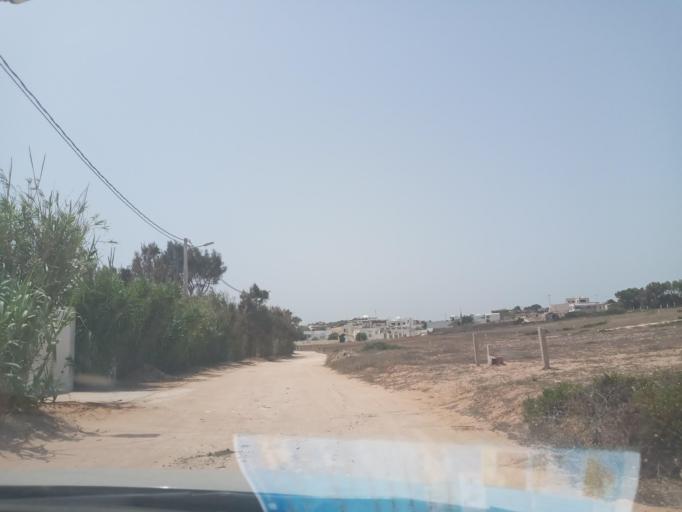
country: TN
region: Nabul
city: El Haouaria
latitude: 37.0303
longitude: 11.0566
